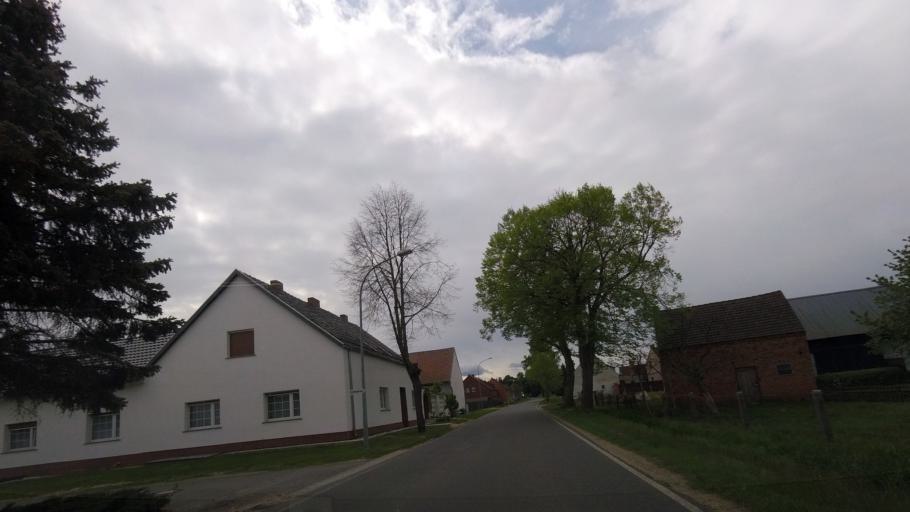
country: DE
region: Brandenburg
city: Dahme
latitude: 51.8965
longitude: 13.4104
